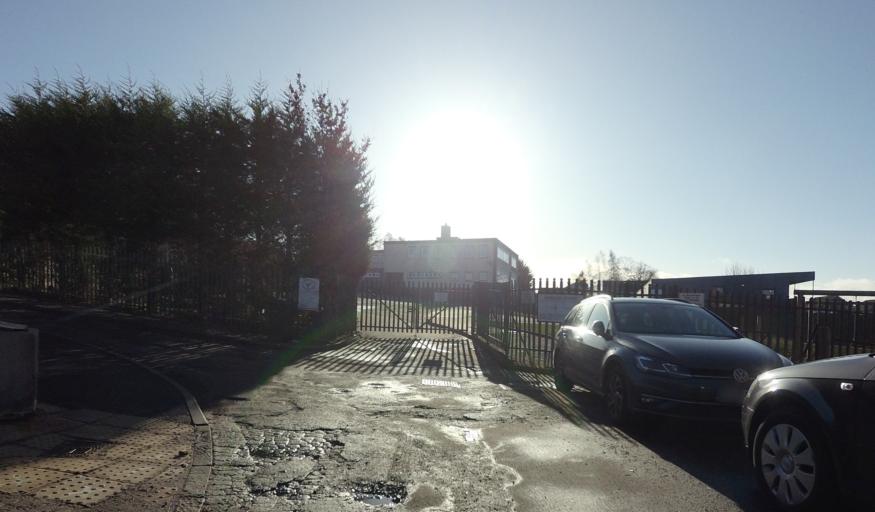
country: GB
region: Scotland
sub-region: Edinburgh
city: Colinton
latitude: 55.9529
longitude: -3.2808
